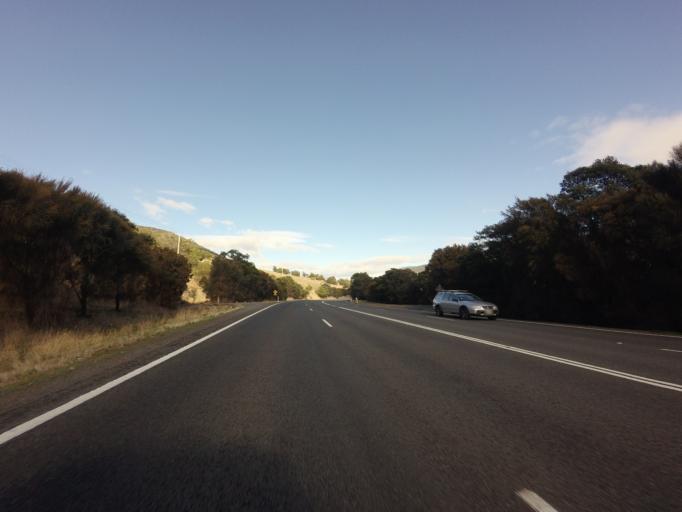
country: AU
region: Tasmania
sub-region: Glenorchy
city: Granton
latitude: -42.7524
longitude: 147.1699
